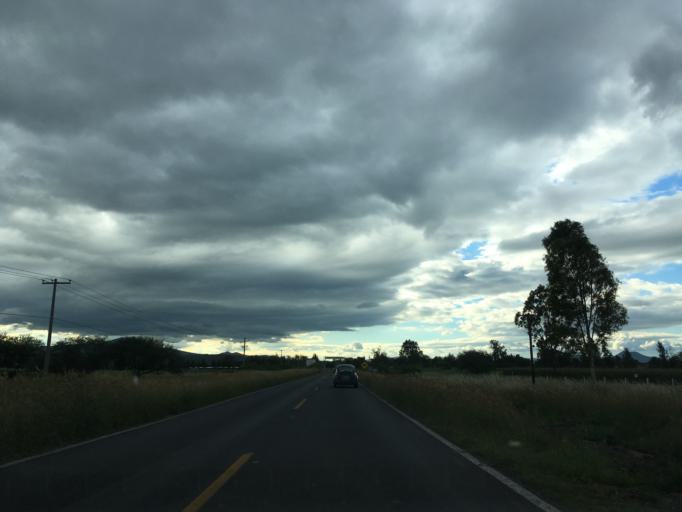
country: MX
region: Michoacan
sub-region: Cuitzeo
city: Cuamio
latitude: 20.0732
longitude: -101.1253
